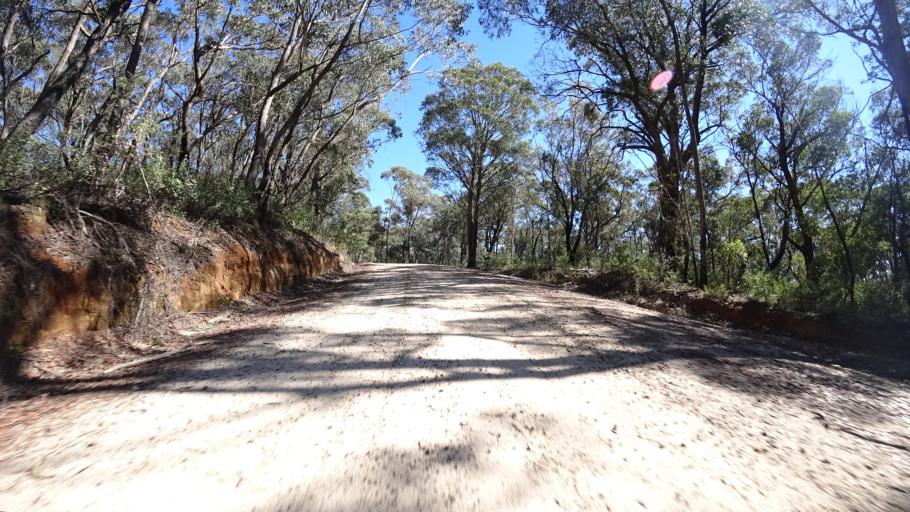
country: AU
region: New South Wales
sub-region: Lithgow
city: Lithgow
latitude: -33.4815
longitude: 150.2552
